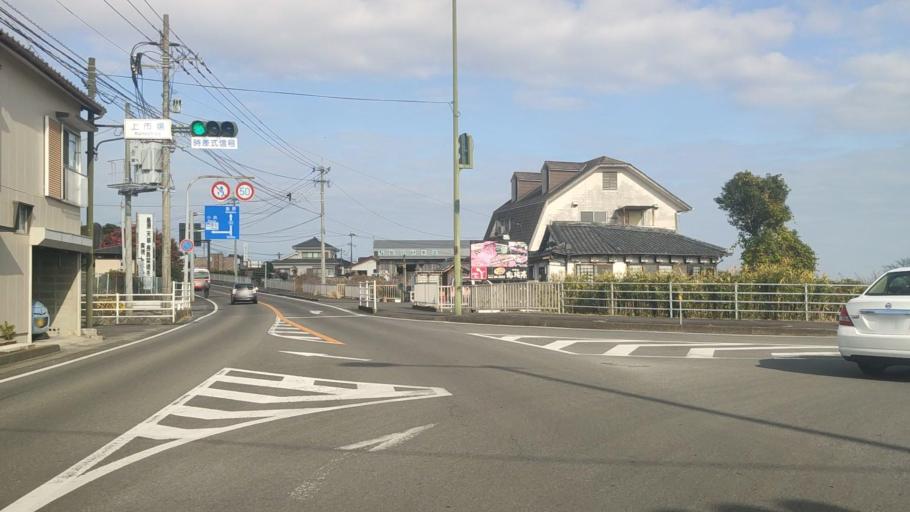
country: JP
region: Nagasaki
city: Shimabara
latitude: 32.7210
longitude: 130.3547
